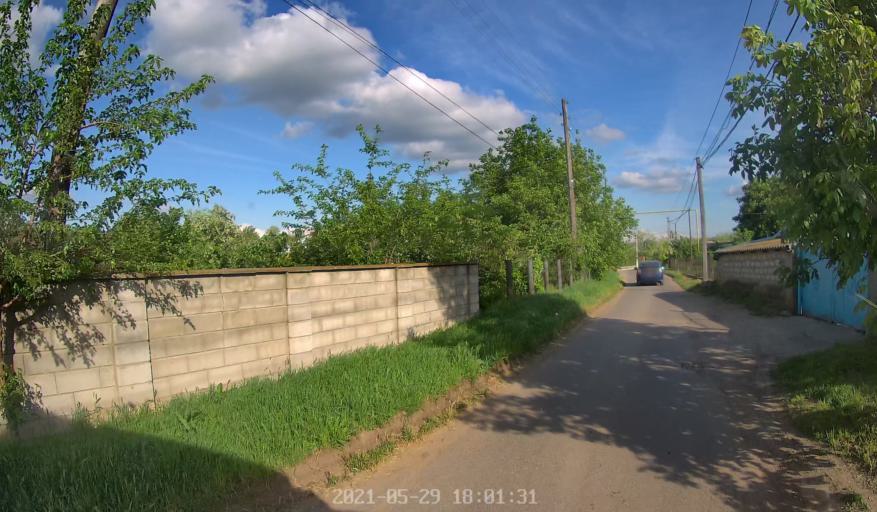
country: MD
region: Laloveni
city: Ialoveni
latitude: 46.8374
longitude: 28.8488
